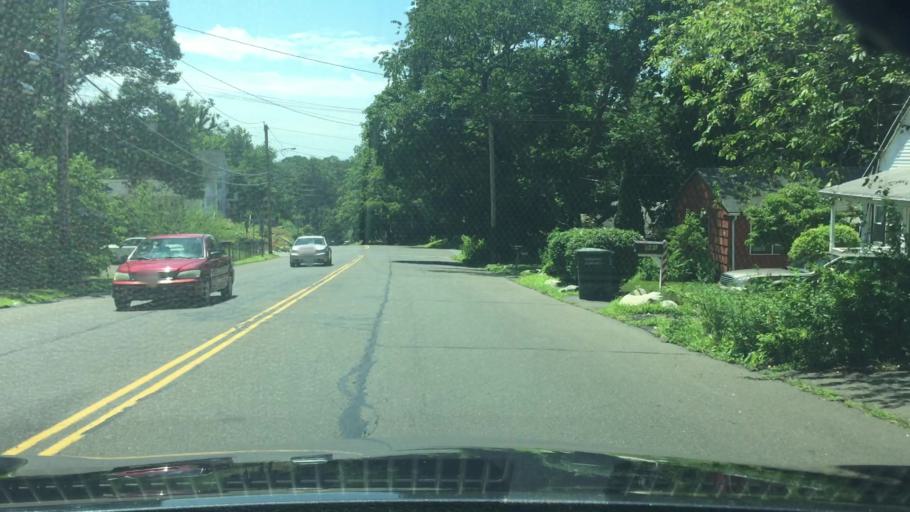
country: US
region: Connecticut
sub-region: Fairfield County
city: Trumbull
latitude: 41.2156
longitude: -73.2023
